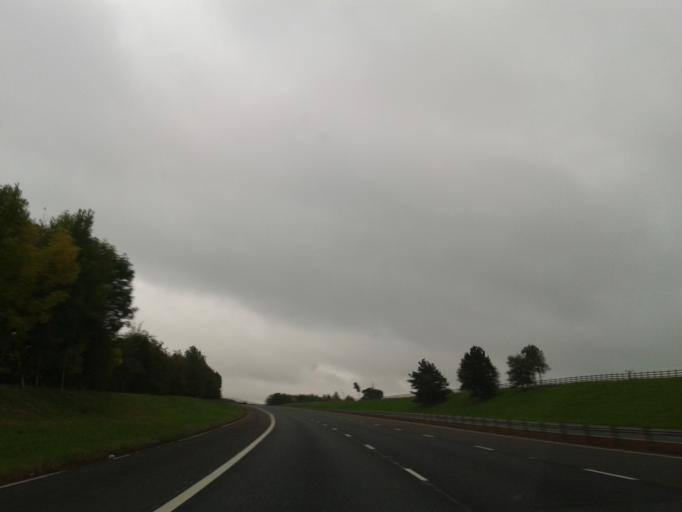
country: GB
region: Scotland
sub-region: Dumfries and Galloway
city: Lochmaben
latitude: 55.1770
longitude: -3.4023
